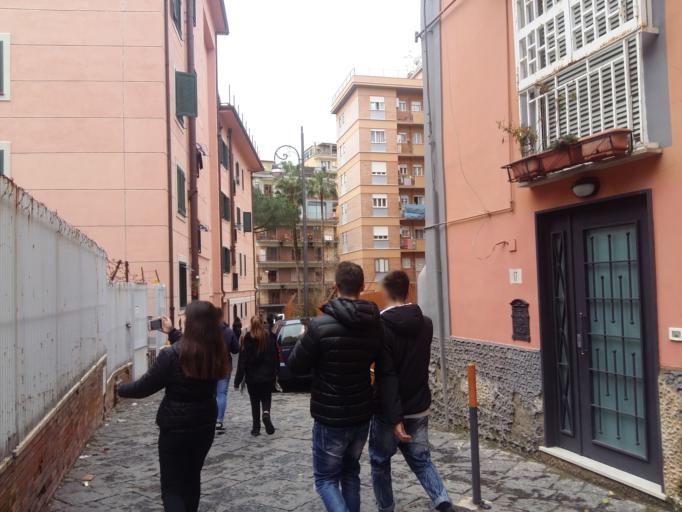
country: IT
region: Campania
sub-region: Provincia di Napoli
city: Napoli
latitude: 40.8560
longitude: 14.2299
